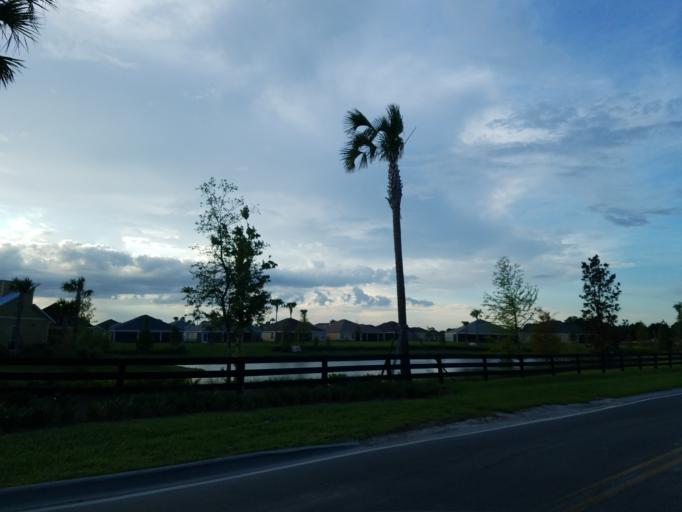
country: US
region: Florida
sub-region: Sumter County
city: Wildwood
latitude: 28.7913
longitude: -82.0208
